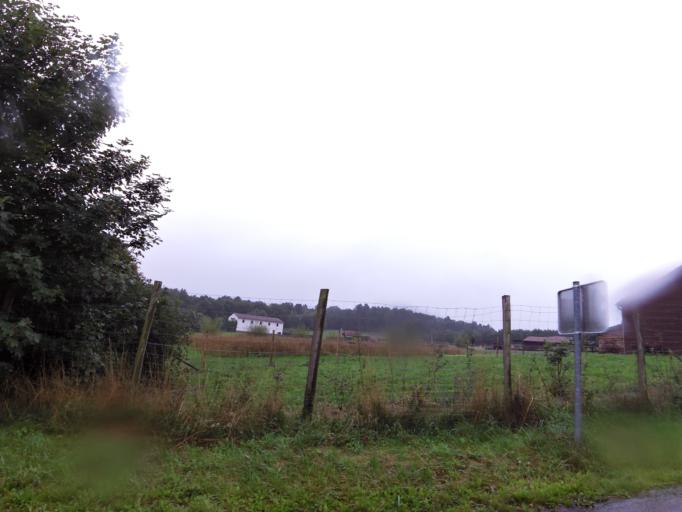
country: BE
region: Wallonia
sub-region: Province de Namur
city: Rochefort
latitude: 50.1637
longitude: 5.2419
